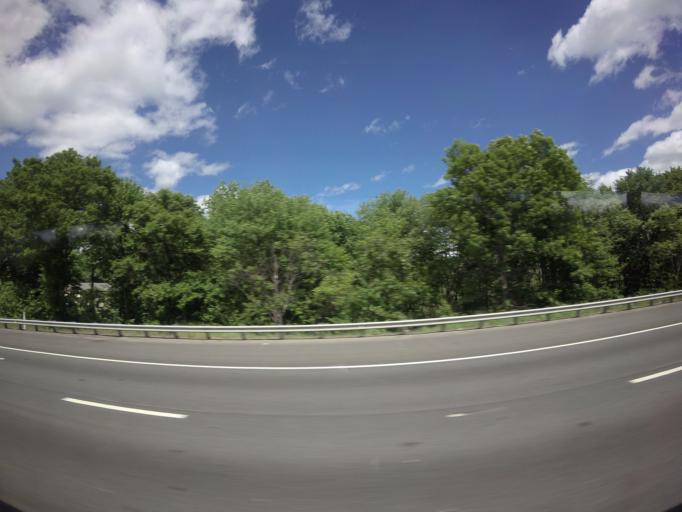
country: US
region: Massachusetts
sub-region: Middlesex County
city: Wilmington
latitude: 42.5452
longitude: -71.1355
